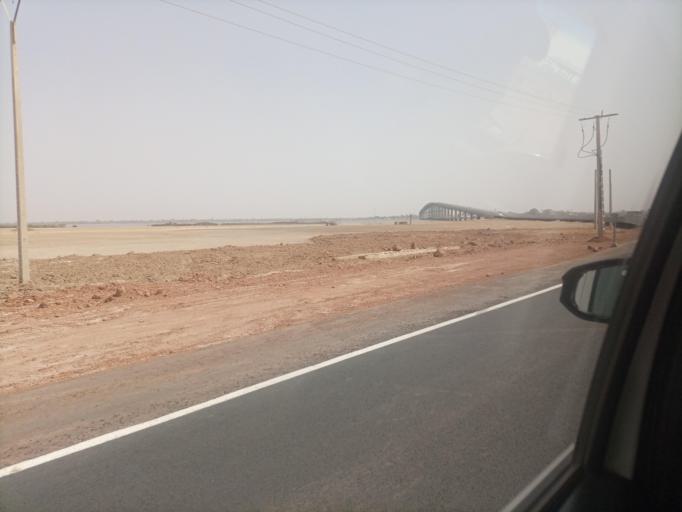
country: SN
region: Fatick
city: Foundiougne
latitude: 14.1449
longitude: -16.4721
